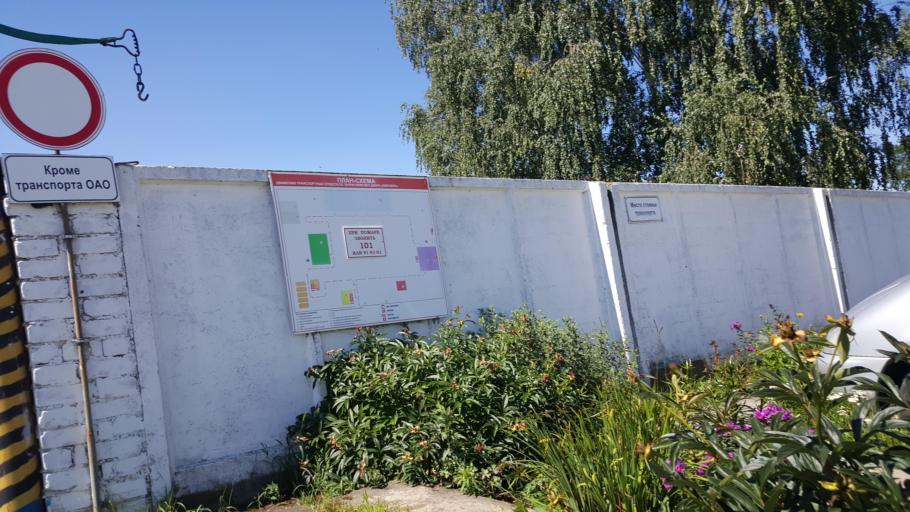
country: BY
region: Brest
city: Charnawchytsy
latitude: 52.2244
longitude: 23.7833
